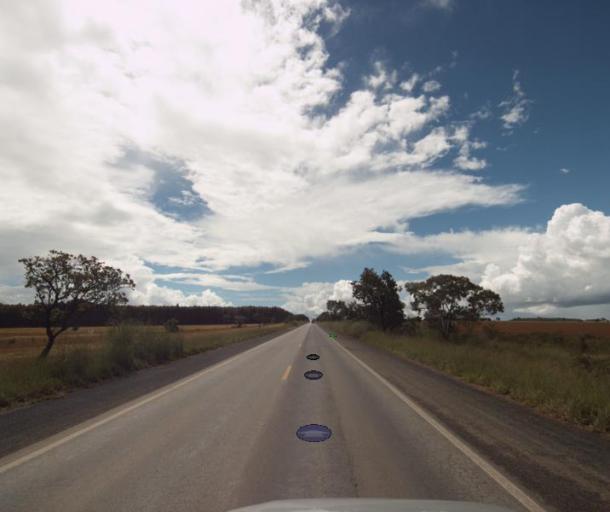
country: BR
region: Goias
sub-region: Uruacu
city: Uruacu
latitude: -14.1783
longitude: -49.1257
